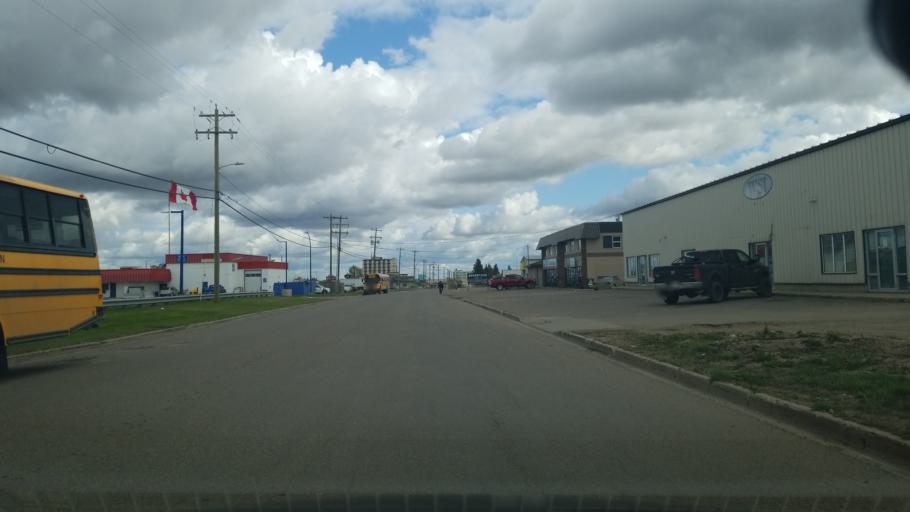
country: CA
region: Saskatchewan
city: Lloydminster
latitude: 53.2768
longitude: -110.0296
